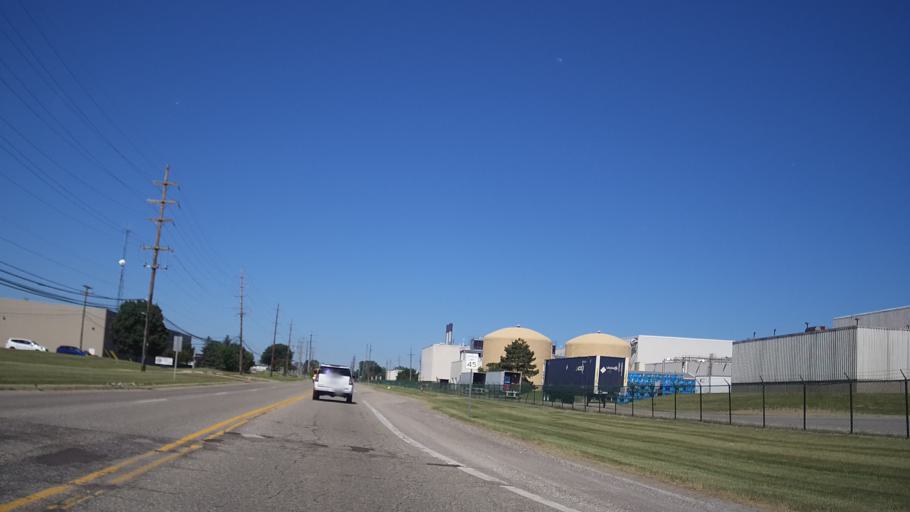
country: US
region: Michigan
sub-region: Macomb County
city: Sterling Heights
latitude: 42.5950
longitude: -83.0324
